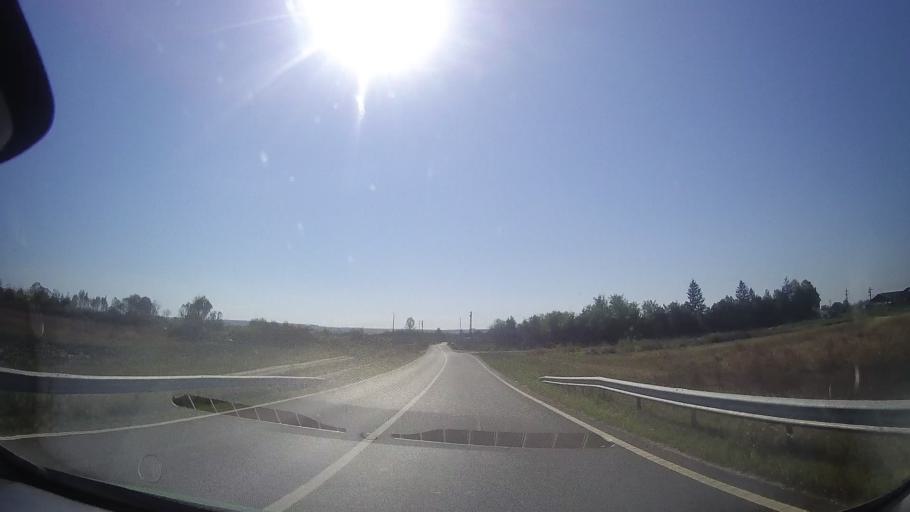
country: RO
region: Timis
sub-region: Comuna Bethausen
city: Bethausen
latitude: 45.8136
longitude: 21.9590
